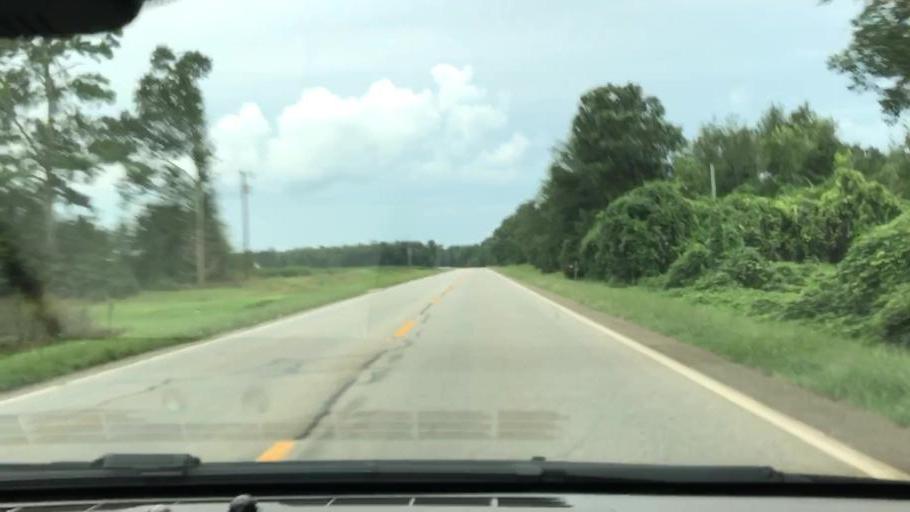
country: US
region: Georgia
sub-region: Early County
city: Blakely
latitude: 31.3163
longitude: -85.0373
